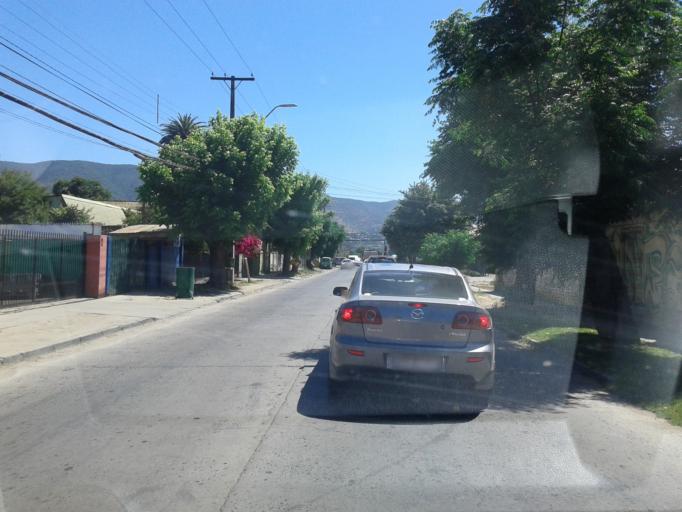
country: CL
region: Valparaiso
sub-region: Provincia de Marga Marga
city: Limache
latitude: -33.0093
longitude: -71.2511
